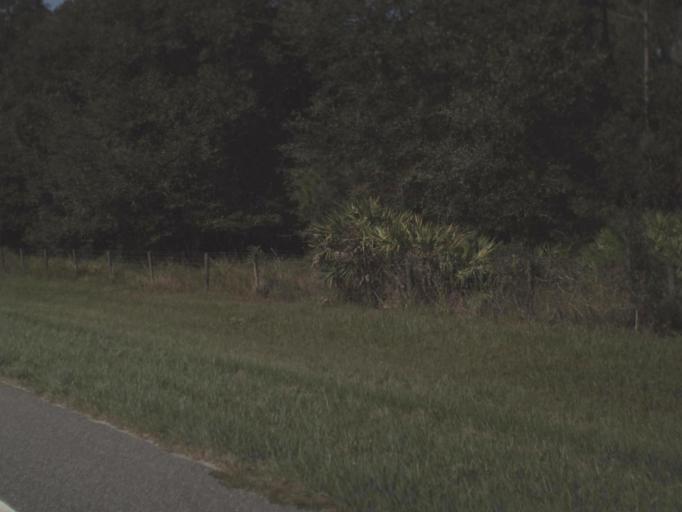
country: US
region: Florida
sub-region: Highlands County
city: Avon Park
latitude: 27.5705
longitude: -81.6281
